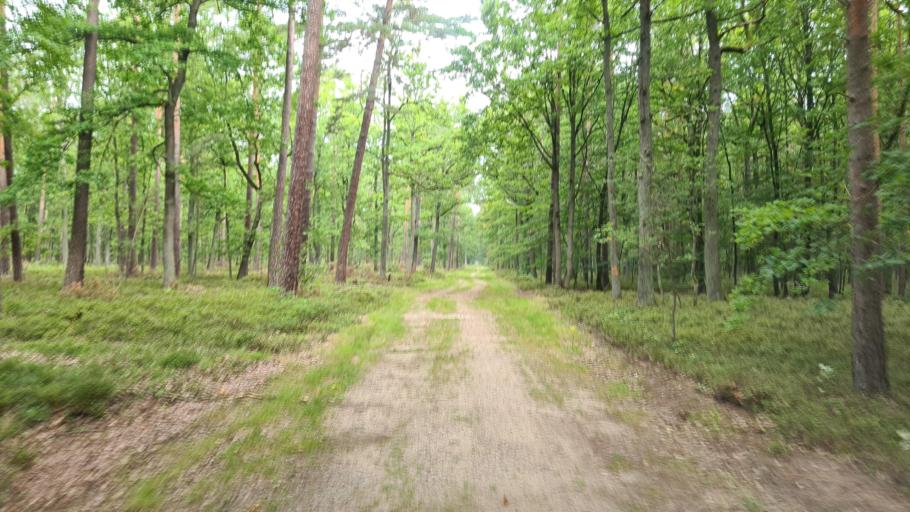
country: DE
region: Brandenburg
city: Hohenbucko
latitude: 51.7796
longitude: 13.5474
